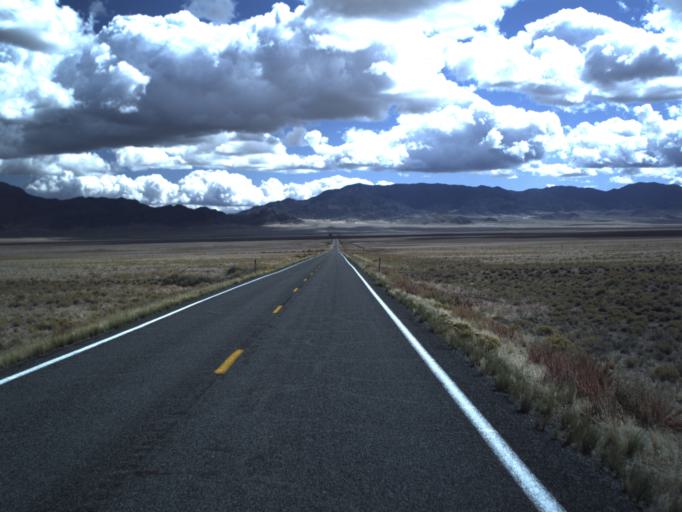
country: US
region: Utah
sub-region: Beaver County
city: Milford
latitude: 38.5569
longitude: -113.7486
